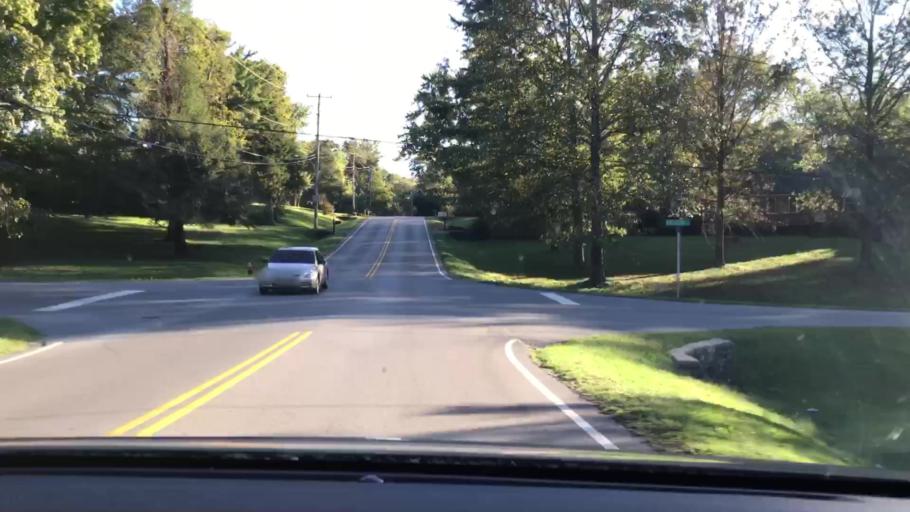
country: US
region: Tennessee
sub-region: Davidson County
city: Oak Hill
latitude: 36.0683
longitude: -86.6963
